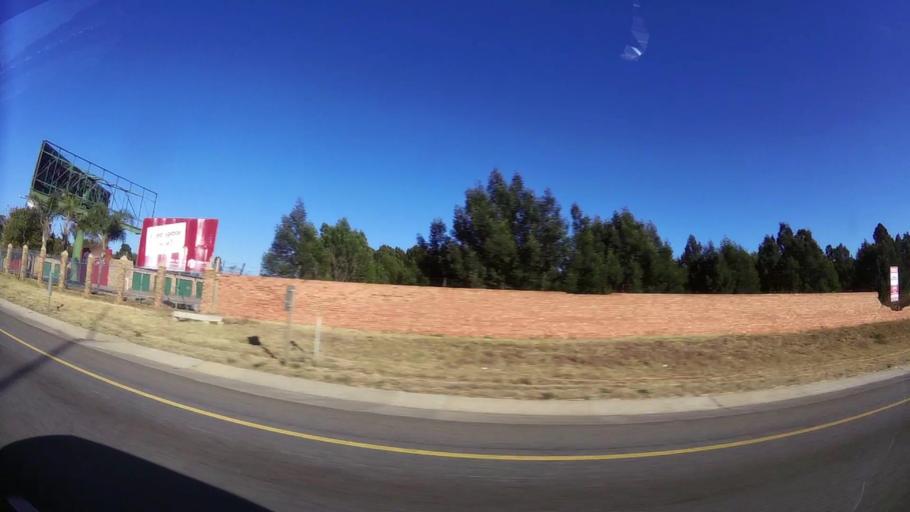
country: ZA
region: Gauteng
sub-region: City of Tshwane Metropolitan Municipality
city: Centurion
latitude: -25.8976
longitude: 28.2545
